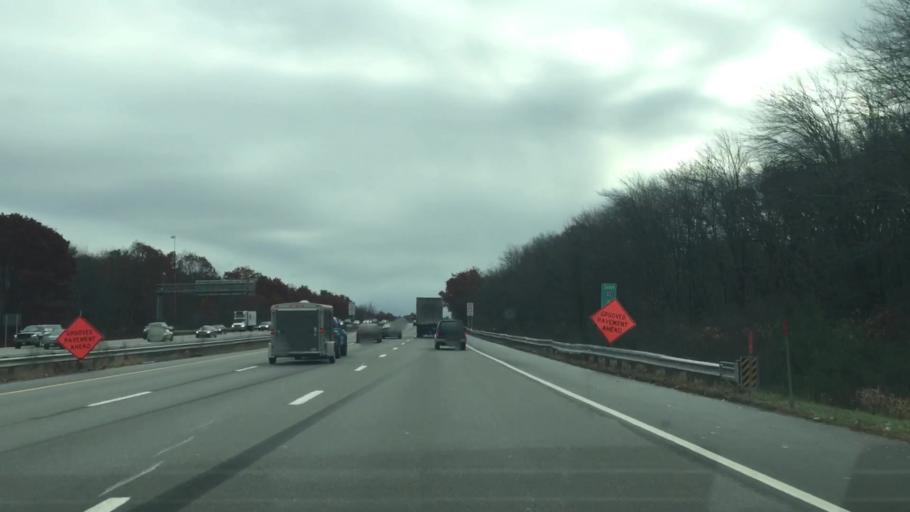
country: US
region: Massachusetts
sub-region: Essex County
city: Methuen
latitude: 42.7482
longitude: -71.2150
